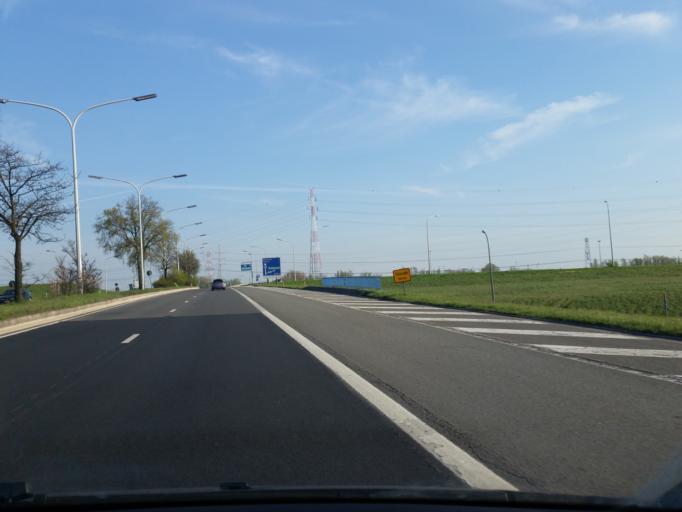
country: BE
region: Flanders
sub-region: Provincie Oost-Vlaanderen
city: Sint-Niklaas
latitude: 51.1433
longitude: 4.1669
